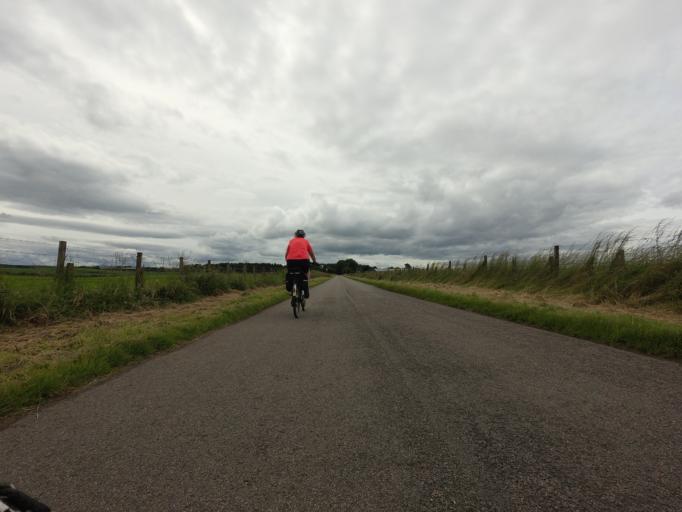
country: GB
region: Scotland
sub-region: Moray
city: Forres
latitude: 57.6050
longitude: -3.7343
